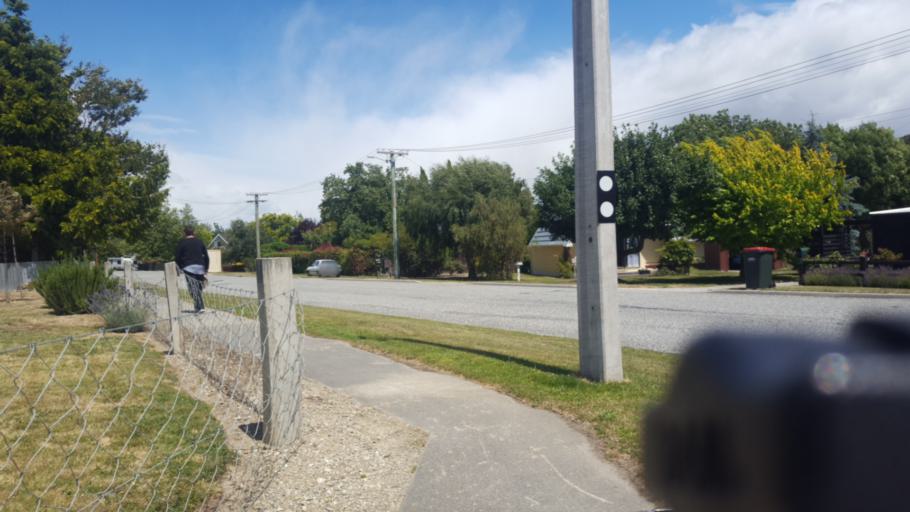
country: NZ
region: Otago
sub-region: Queenstown-Lakes District
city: Wanaka
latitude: -45.1905
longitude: 169.3178
